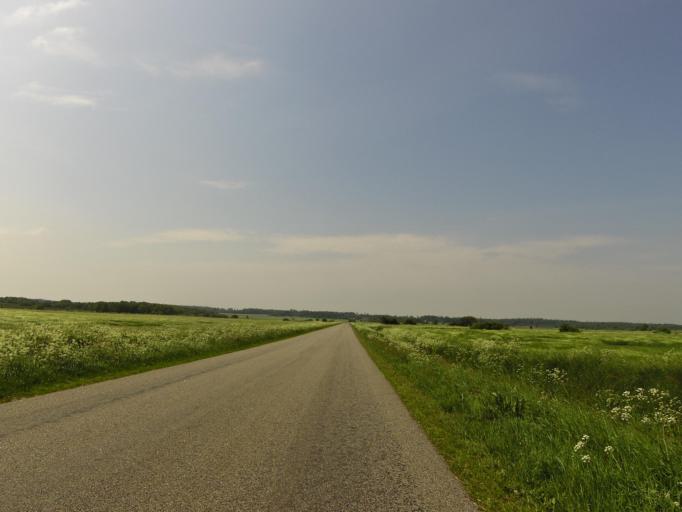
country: DK
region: South Denmark
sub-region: Tonder Kommune
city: Toftlund
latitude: 55.1917
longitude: 8.9966
